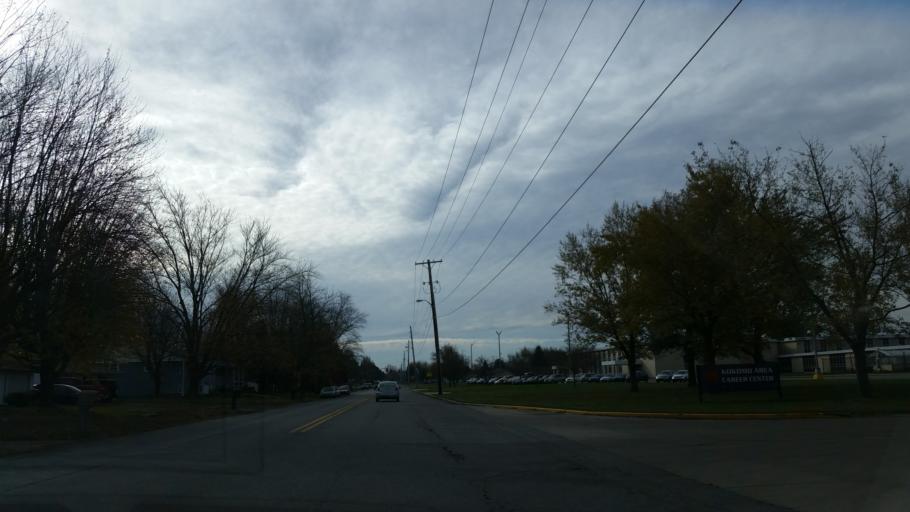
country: US
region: Indiana
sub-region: Howard County
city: Kokomo
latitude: 40.4575
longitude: -86.1556
